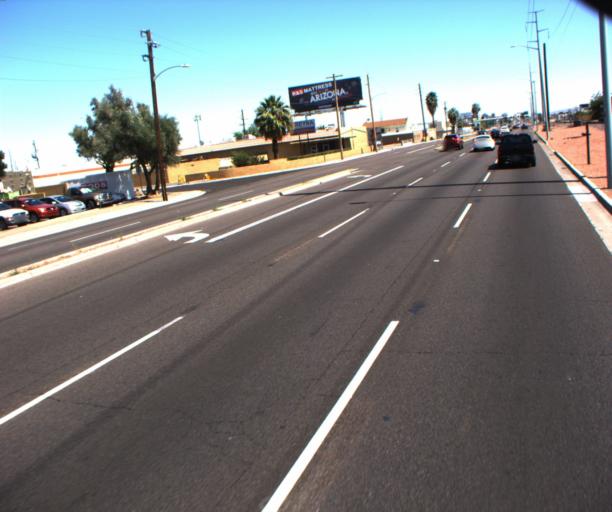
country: US
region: Arizona
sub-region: Maricopa County
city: Phoenix
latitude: 33.4899
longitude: -112.1285
